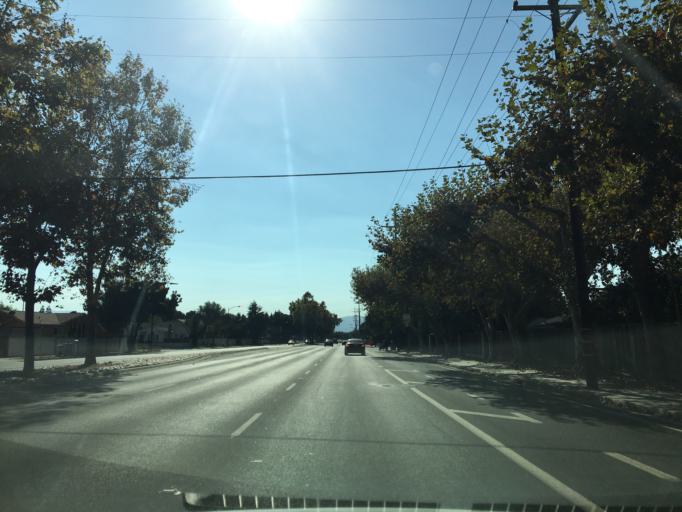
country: US
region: California
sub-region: Santa Clara County
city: Alum Rock
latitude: 37.3768
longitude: -121.8704
